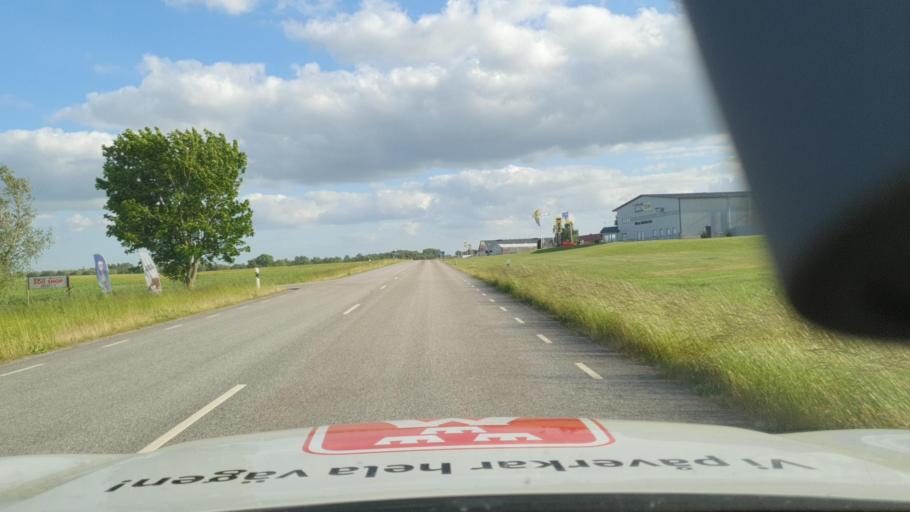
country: SE
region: Skane
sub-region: Tomelilla Kommun
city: Tomelilla
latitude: 55.5552
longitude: 13.9604
